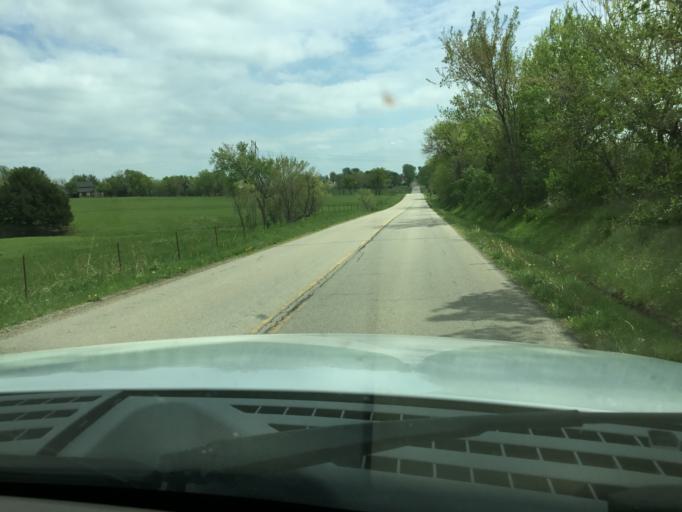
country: US
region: Kansas
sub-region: Shawnee County
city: Auburn
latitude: 38.9707
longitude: -95.8058
